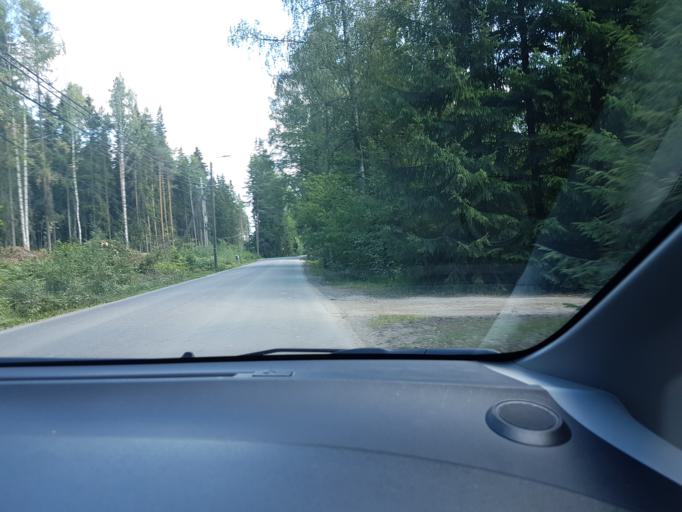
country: FI
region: Uusimaa
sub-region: Helsinki
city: Kilo
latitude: 60.3371
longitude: 24.7921
